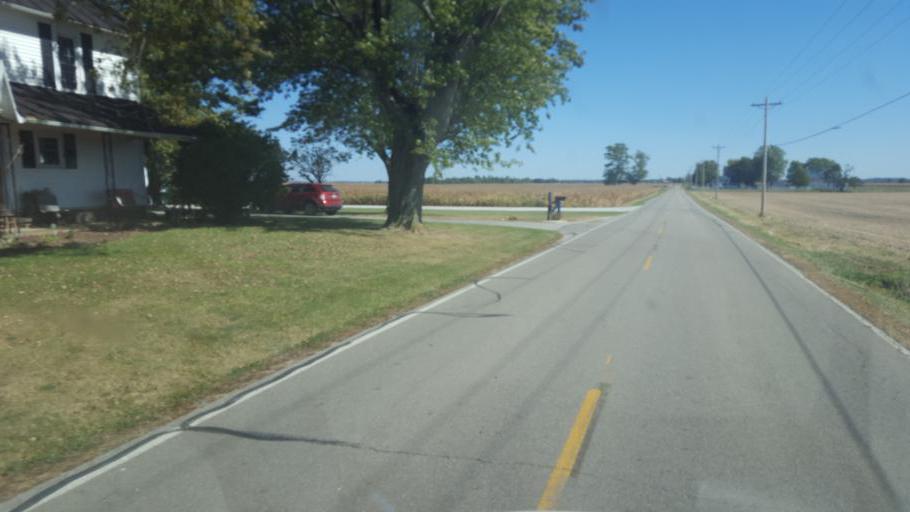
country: US
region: Ohio
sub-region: Huron County
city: Willard
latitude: 40.9820
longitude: -82.7755
